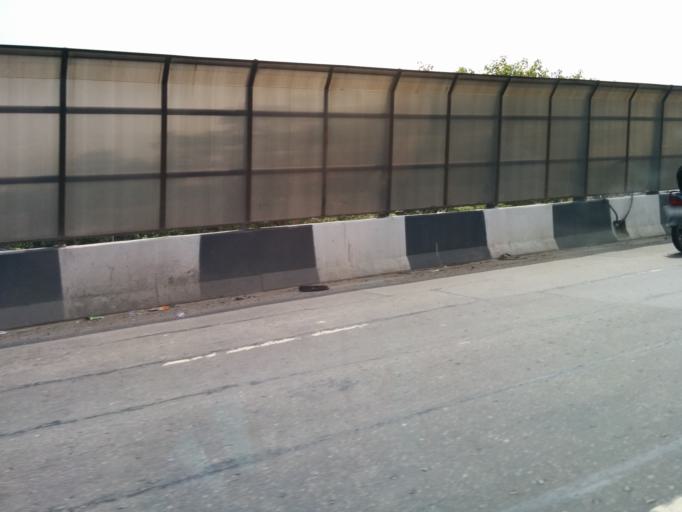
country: IN
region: NCT
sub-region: New Delhi
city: New Delhi
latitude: 28.5505
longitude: 77.1840
